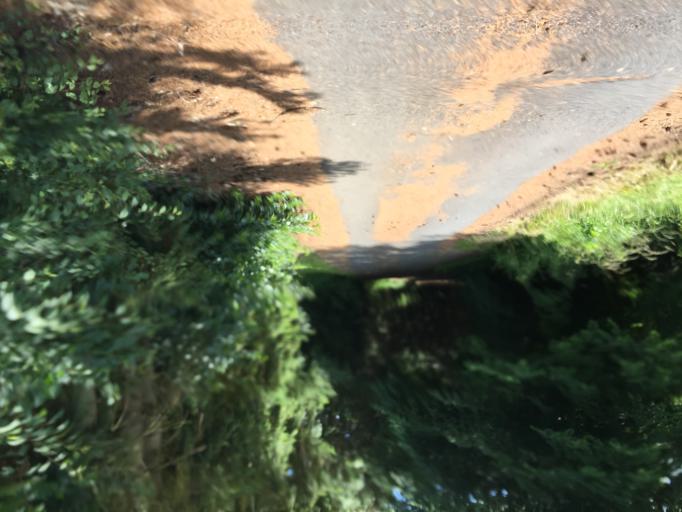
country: DE
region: Rheinland-Pfalz
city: Grossholbach
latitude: 50.4397
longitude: 7.8851
